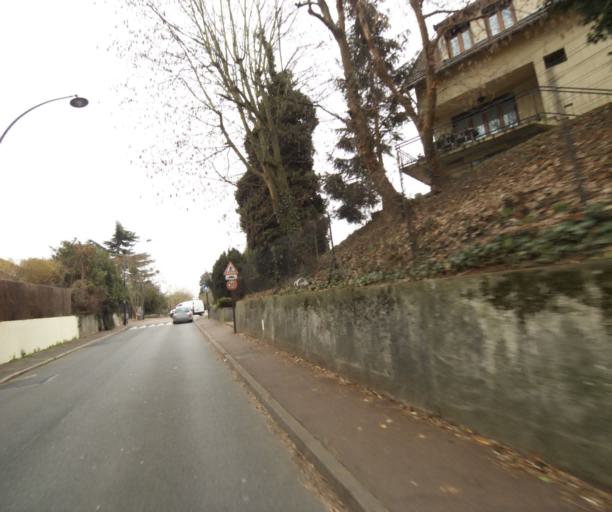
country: FR
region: Ile-de-France
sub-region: Departement des Hauts-de-Seine
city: Rueil-Malmaison
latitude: 48.8664
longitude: 2.1866
